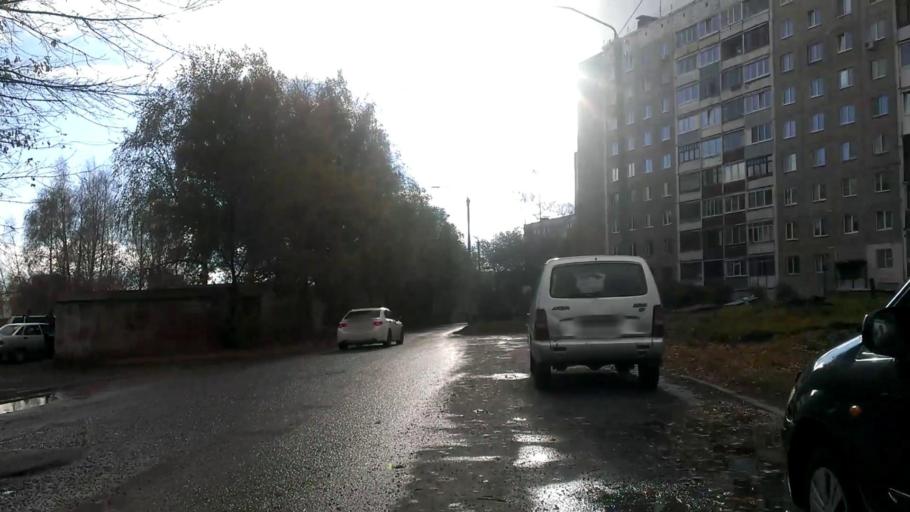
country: RU
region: Altai Krai
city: Novosilikatnyy
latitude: 53.3601
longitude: 83.6811
